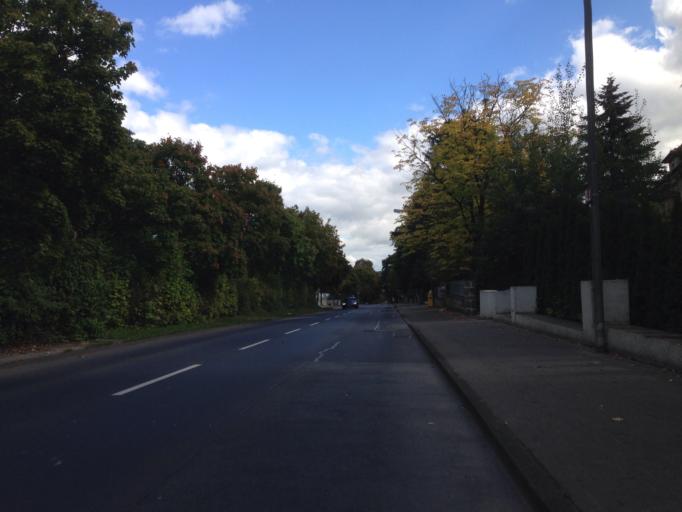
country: DE
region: Hesse
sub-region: Regierungsbezirk Giessen
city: Giessen
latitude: 50.5887
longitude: 8.7114
